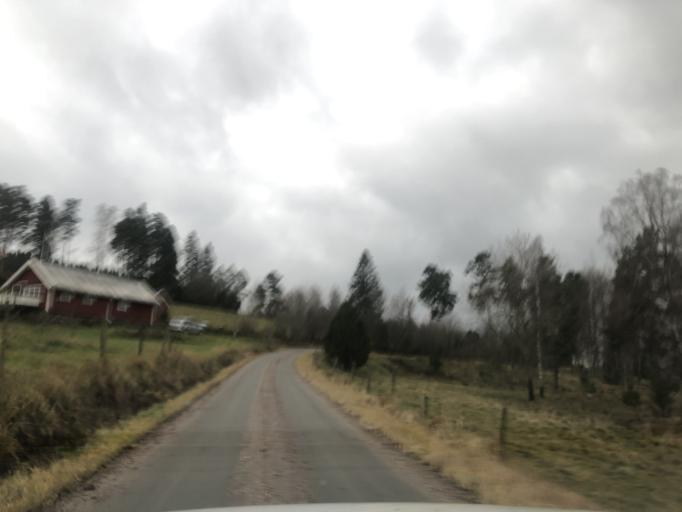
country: SE
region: Vaestra Goetaland
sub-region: Ulricehamns Kommun
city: Ulricehamn
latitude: 57.8885
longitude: 13.4675
